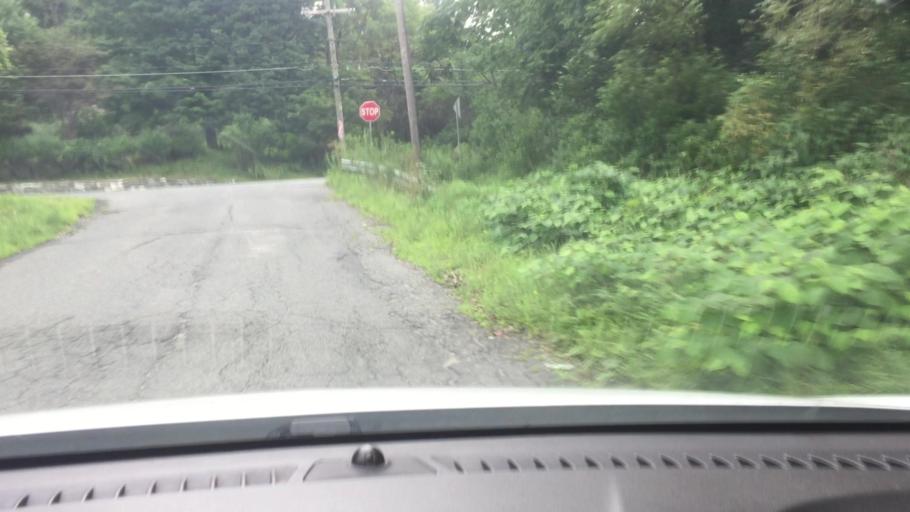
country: US
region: Massachusetts
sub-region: Berkshire County
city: Lanesborough
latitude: 42.5087
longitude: -73.2331
